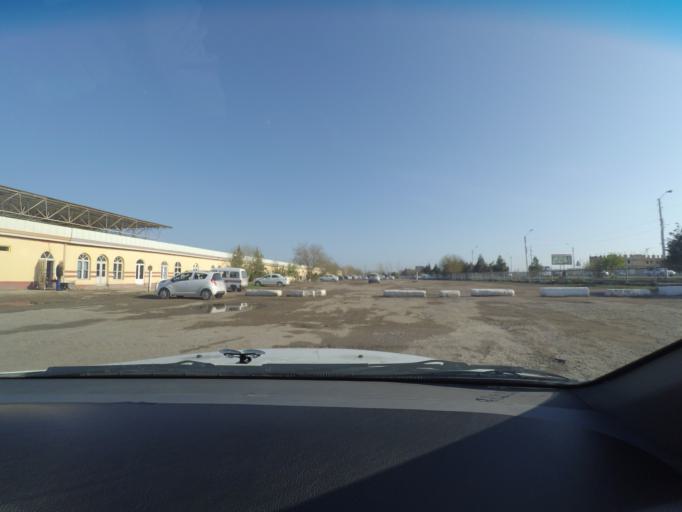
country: UZ
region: Bukhara
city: Bukhara
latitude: 39.8046
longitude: 64.4275
